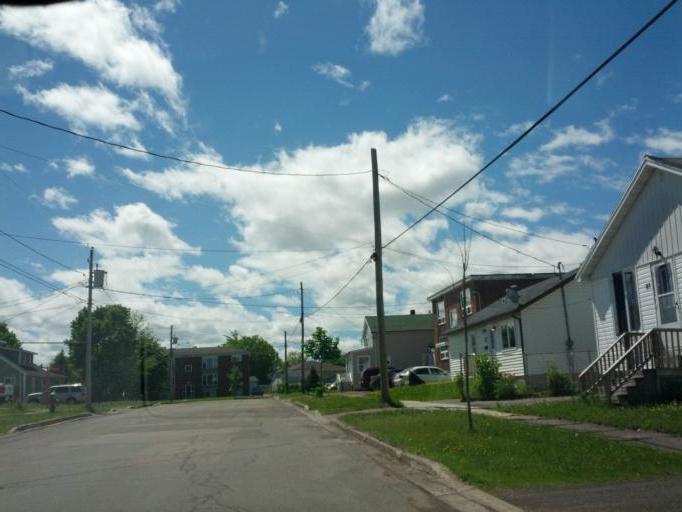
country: CA
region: New Brunswick
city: Moncton
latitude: 46.1145
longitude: -64.7770
